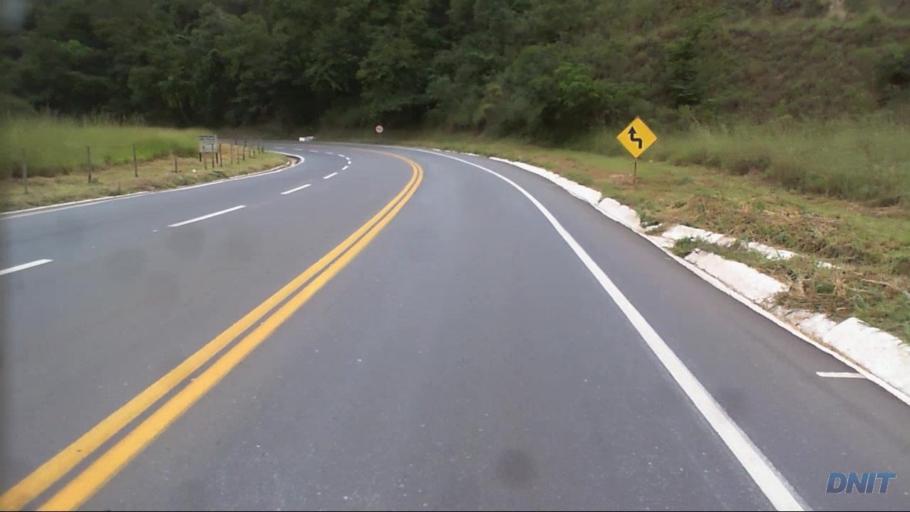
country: BR
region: Minas Gerais
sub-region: Joao Monlevade
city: Joao Monlevade
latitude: -19.8547
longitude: -43.2247
